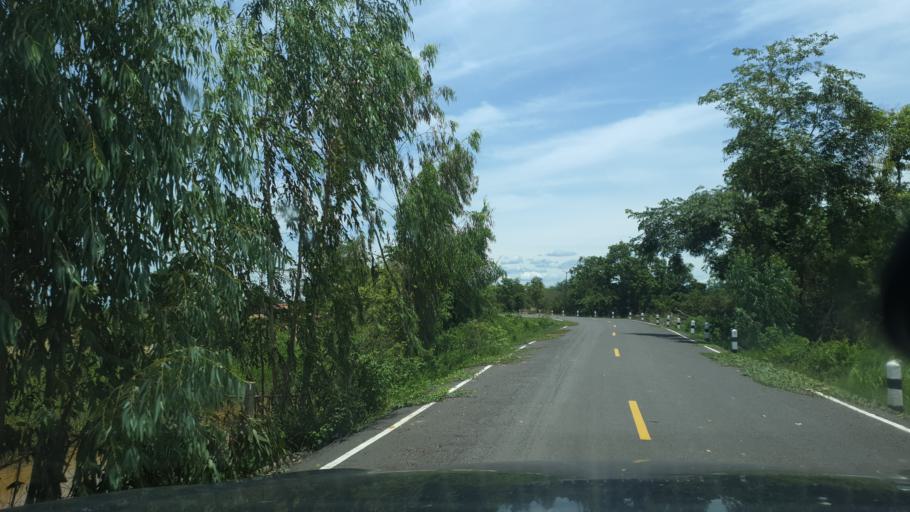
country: TH
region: Sukhothai
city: Ban Na
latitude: 17.1507
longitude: 99.6567
